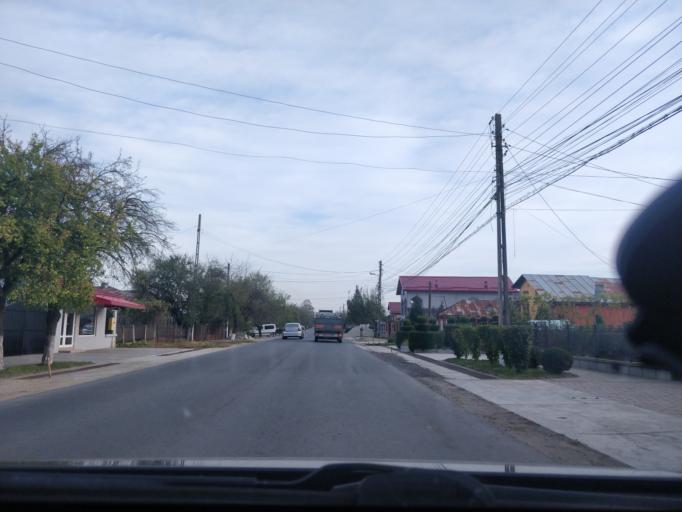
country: RO
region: Giurgiu
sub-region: Comuna Bolintin Vale
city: Malu Spart
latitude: 44.4380
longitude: 25.7199
